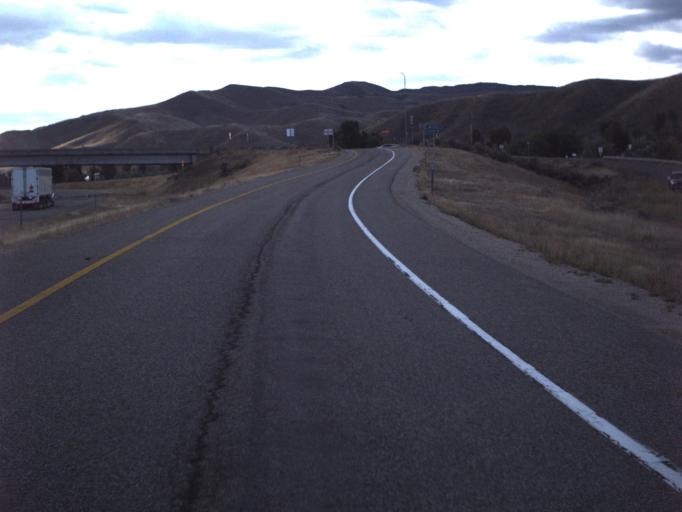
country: US
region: Utah
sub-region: Summit County
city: Coalville
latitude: 41.0177
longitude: -111.4915
